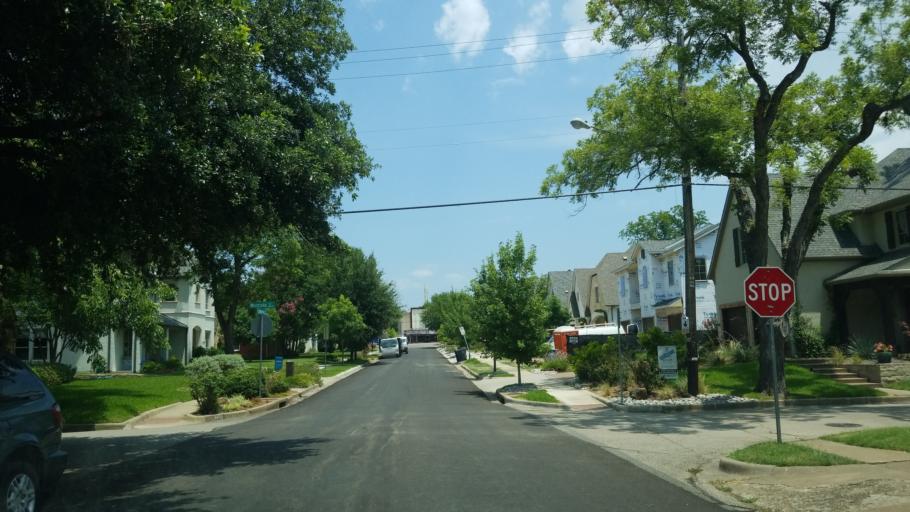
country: US
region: Texas
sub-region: Dallas County
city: Highland Park
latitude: 32.8309
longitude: -96.7724
